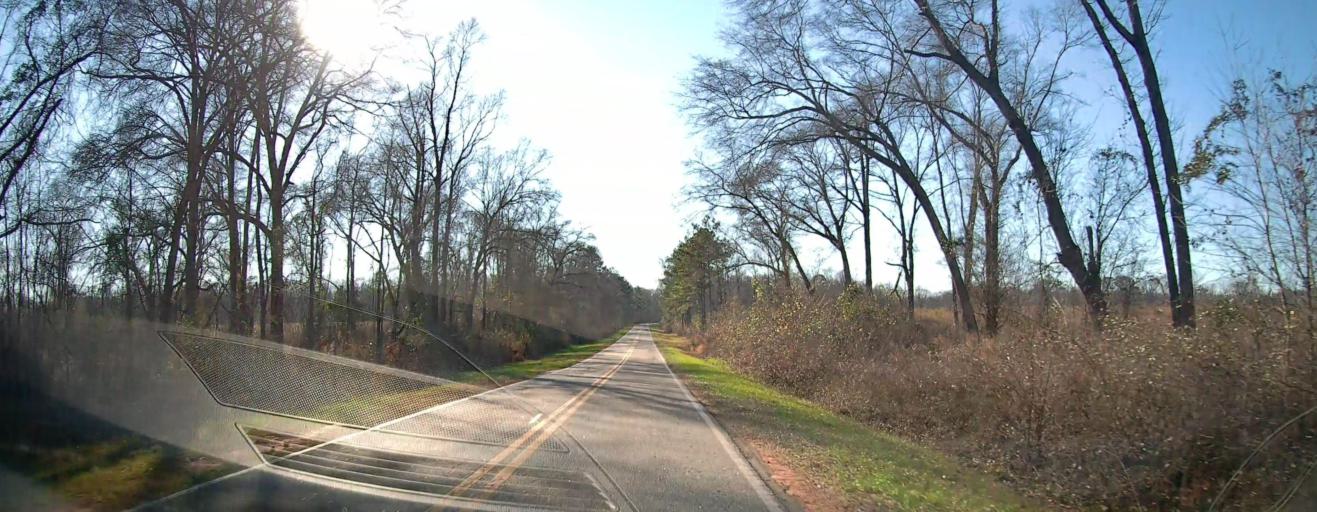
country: US
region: Georgia
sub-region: Sumter County
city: Americus
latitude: 32.0069
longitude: -84.2195
